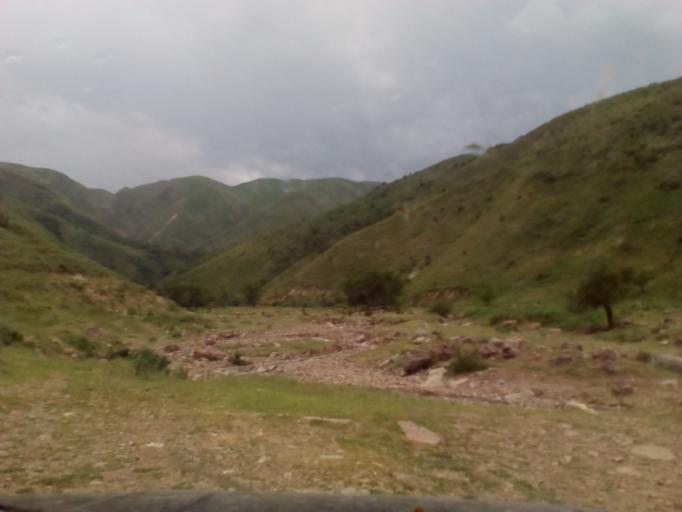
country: KZ
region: Almaty Oblysy
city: Burunday
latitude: 43.1482
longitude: 76.3856
